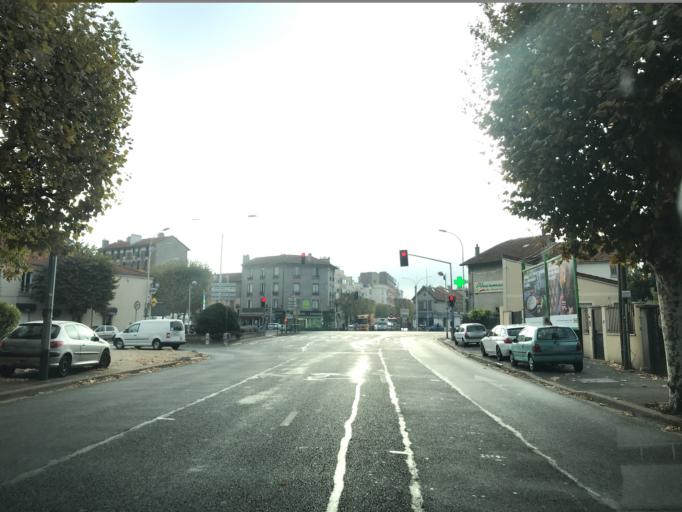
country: FR
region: Ile-de-France
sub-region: Departement du Val-de-Marne
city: Le Perreux-sur-Marne
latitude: 48.8498
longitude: 2.4950
